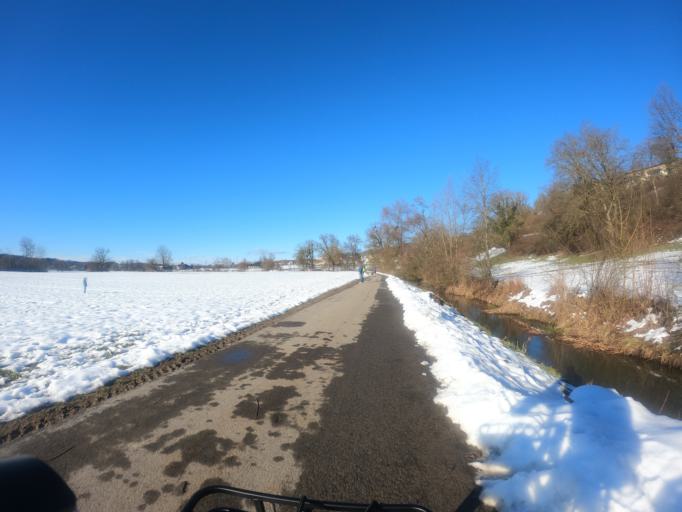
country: CH
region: Aargau
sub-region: Bezirk Bremgarten
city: Unterlunkhofen
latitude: 47.3145
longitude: 8.3844
